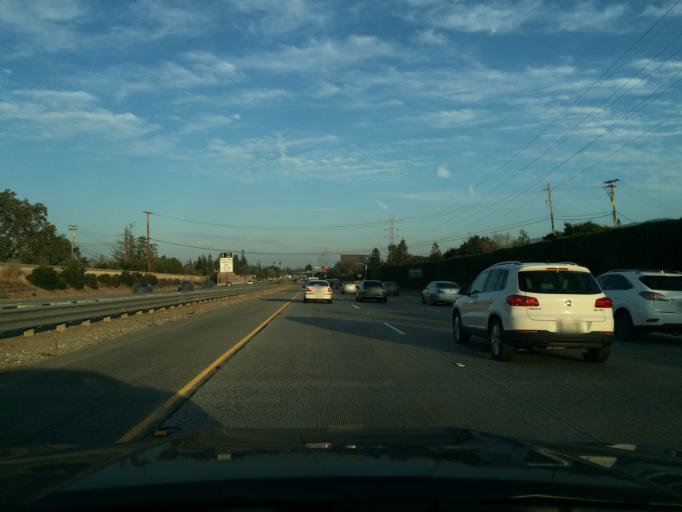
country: US
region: California
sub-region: Santa Clara County
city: Monte Sereno
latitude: 37.2660
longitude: -121.9830
